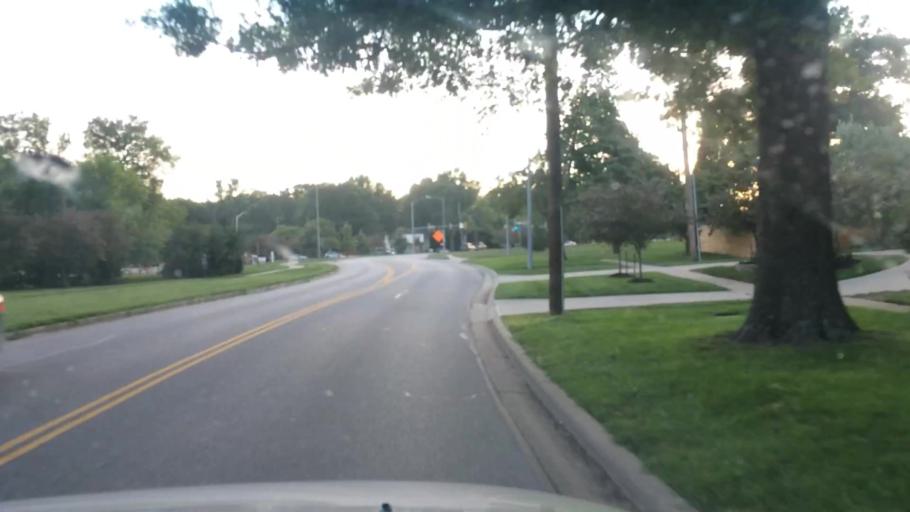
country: US
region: Kansas
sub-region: Johnson County
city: Overland Park
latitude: 38.9646
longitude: -94.6468
